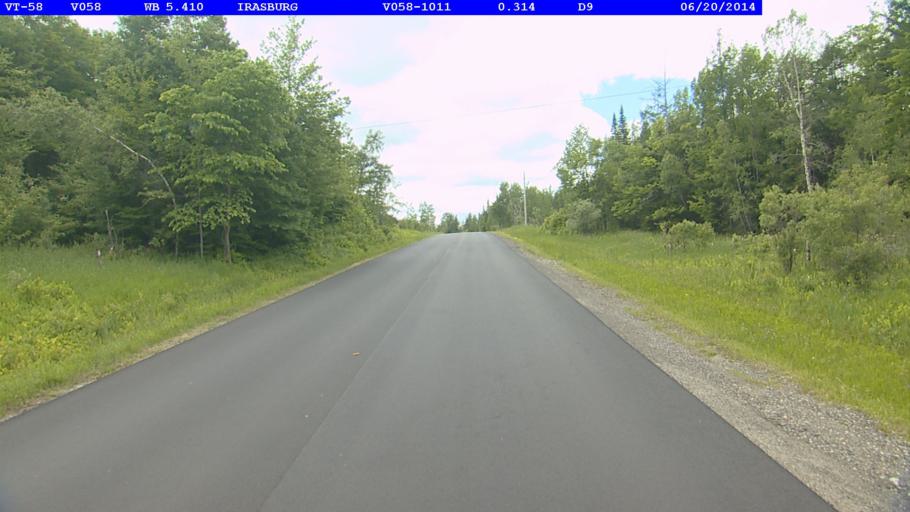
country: US
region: Vermont
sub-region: Orleans County
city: Newport
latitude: 44.8198
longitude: -72.3531
